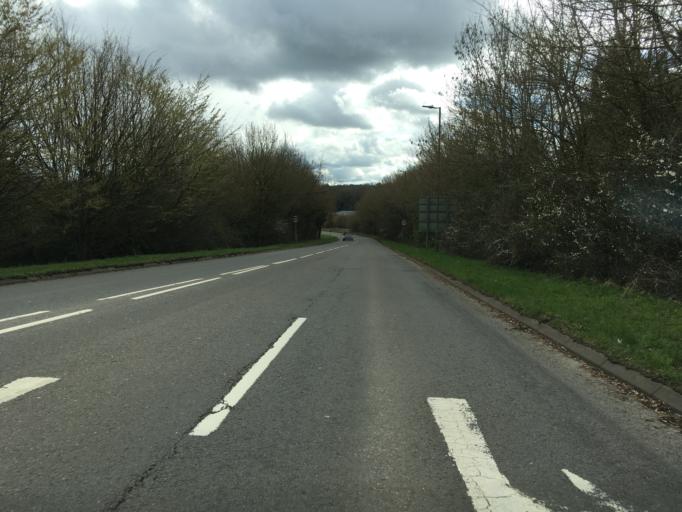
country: GB
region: England
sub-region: Gloucestershire
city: Coleford
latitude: 51.7860
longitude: -2.6139
